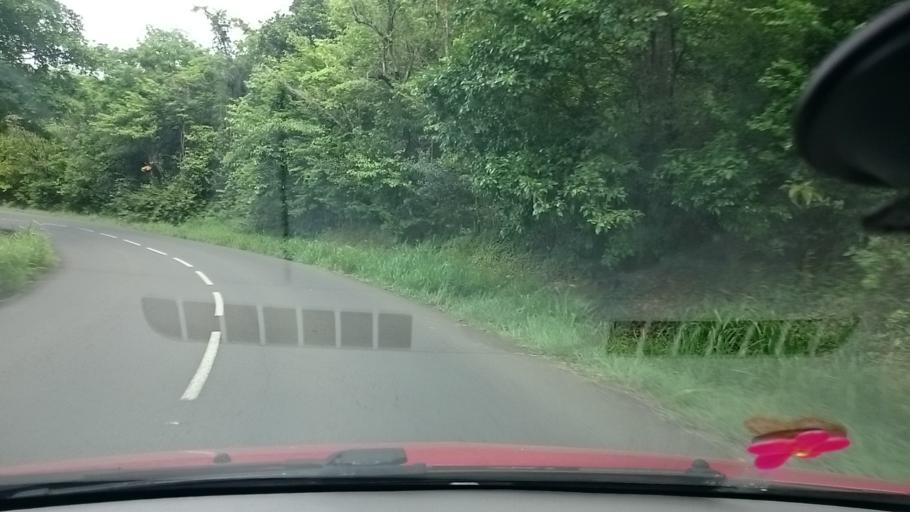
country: MQ
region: Martinique
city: Petite Riviere Salee
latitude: 14.7574
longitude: -60.9286
